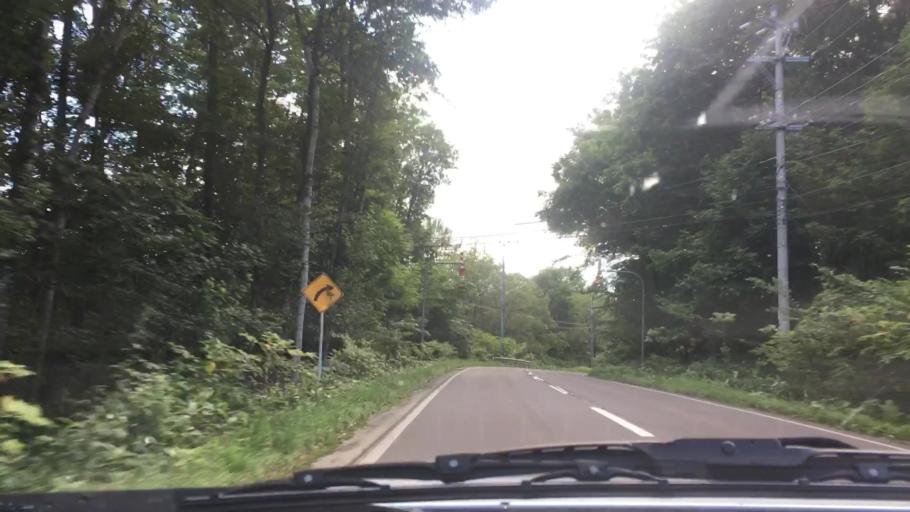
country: JP
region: Hokkaido
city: Otofuke
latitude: 43.1694
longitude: 142.9117
